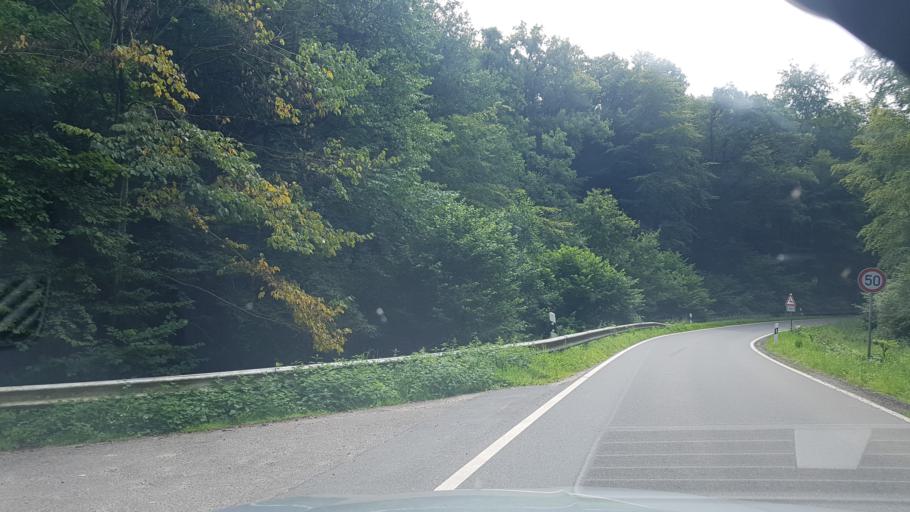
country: DE
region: Schleswig-Holstein
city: Schonbek
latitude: 54.1821
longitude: 9.9618
